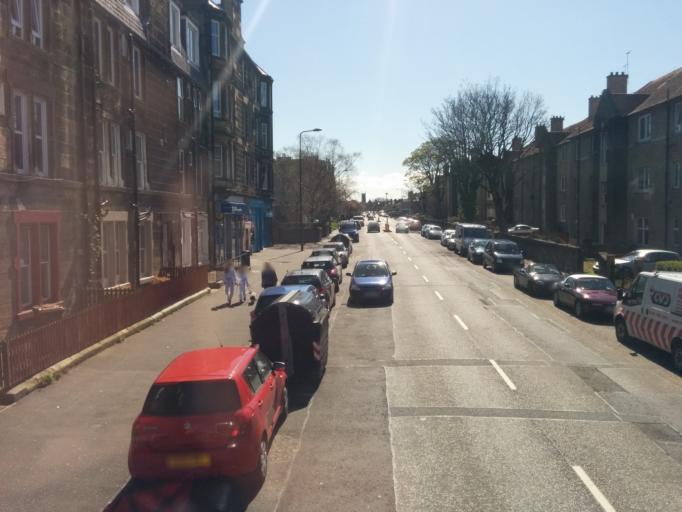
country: GB
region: Scotland
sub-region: Edinburgh
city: Edinburgh
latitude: 55.9769
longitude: -3.2160
